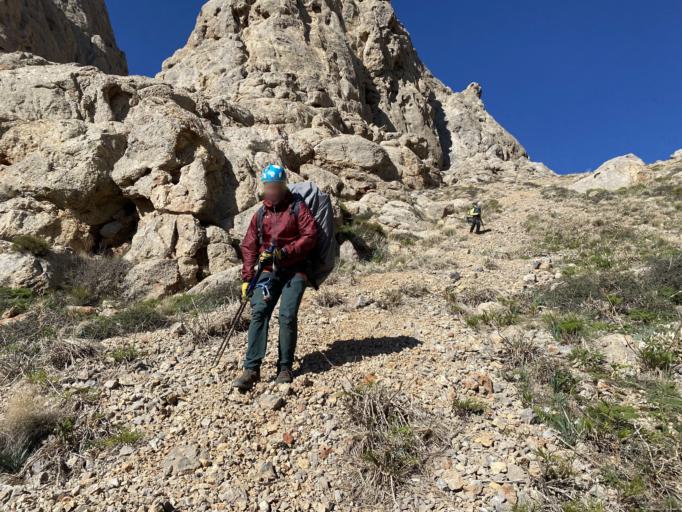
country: KZ
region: Ongtustik Qazaqstan
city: Ashchysay
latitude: 43.7622
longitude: 68.7823
